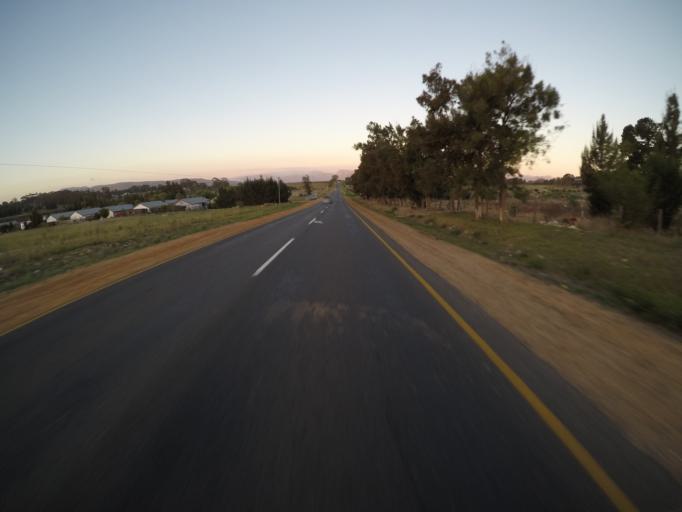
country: ZA
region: Western Cape
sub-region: Cape Winelands District Municipality
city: Paarl
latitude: -33.8071
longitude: 18.8771
